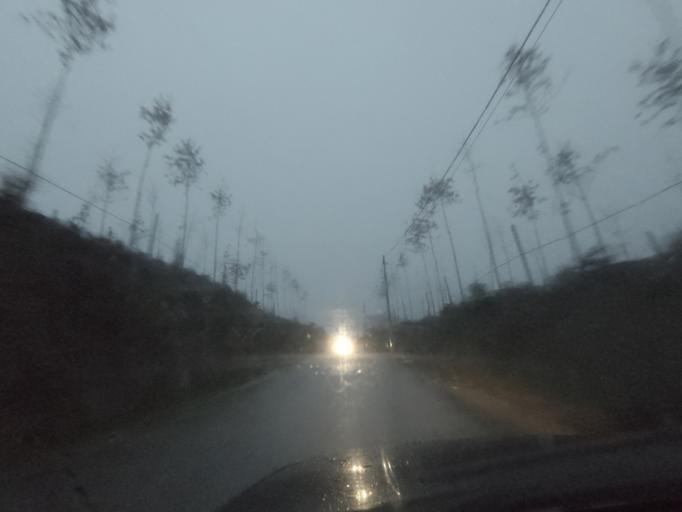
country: PT
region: Vila Real
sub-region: Sabrosa
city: Sabrosa
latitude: 41.2560
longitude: -7.5971
